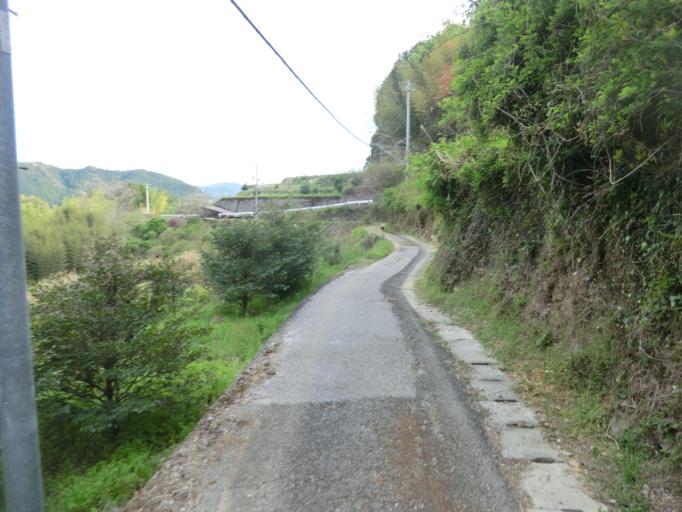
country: JP
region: Kochi
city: Kochi-shi
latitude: 33.6431
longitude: 133.7190
